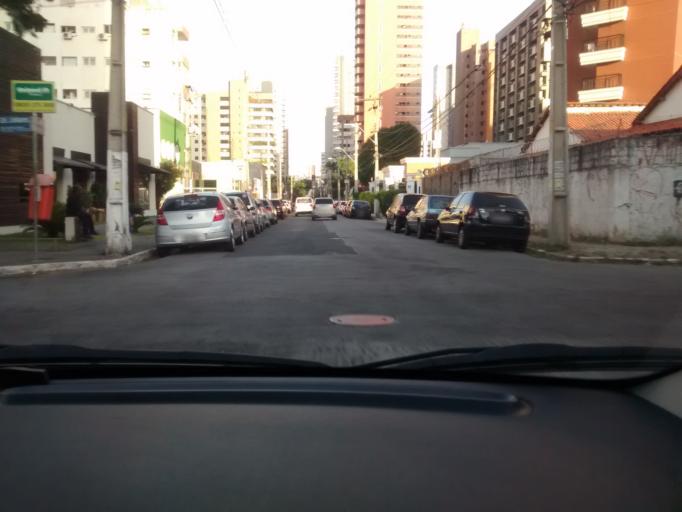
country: BR
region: Ceara
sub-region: Fortaleza
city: Fortaleza
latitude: -3.7395
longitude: -38.4951
